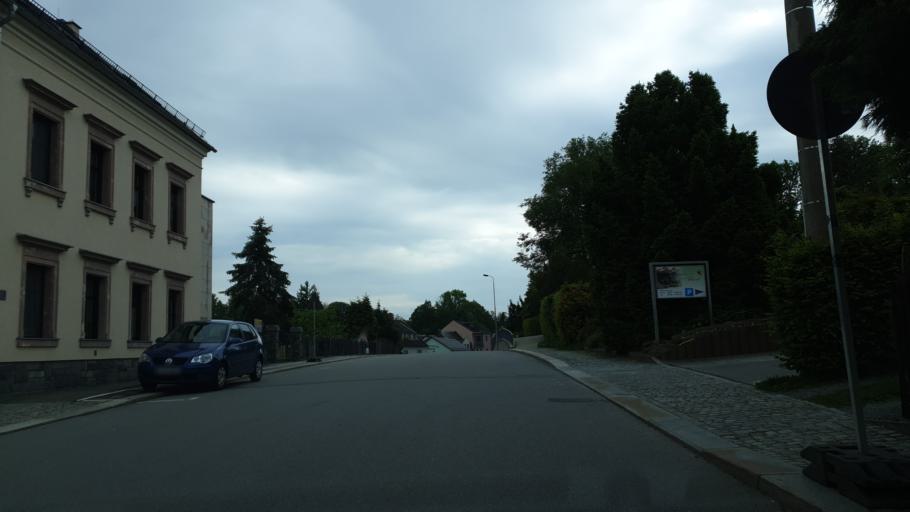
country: DE
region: Saxony
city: Stollberg
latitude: 50.7050
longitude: 12.7760
